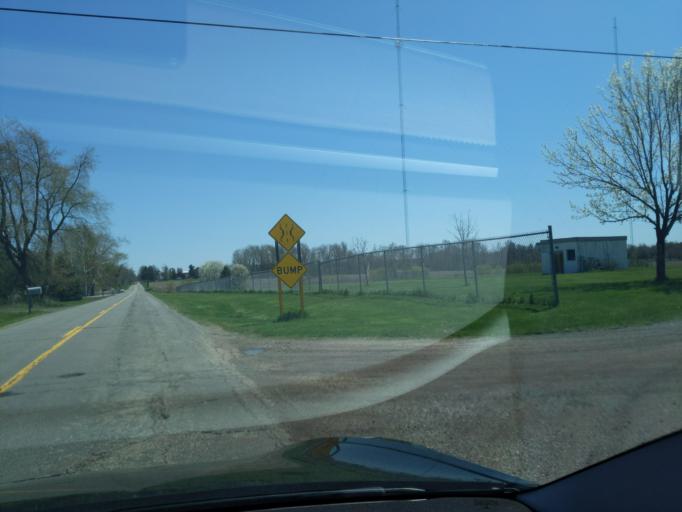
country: US
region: Michigan
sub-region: Ingham County
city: Holt
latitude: 42.5530
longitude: -84.5525
